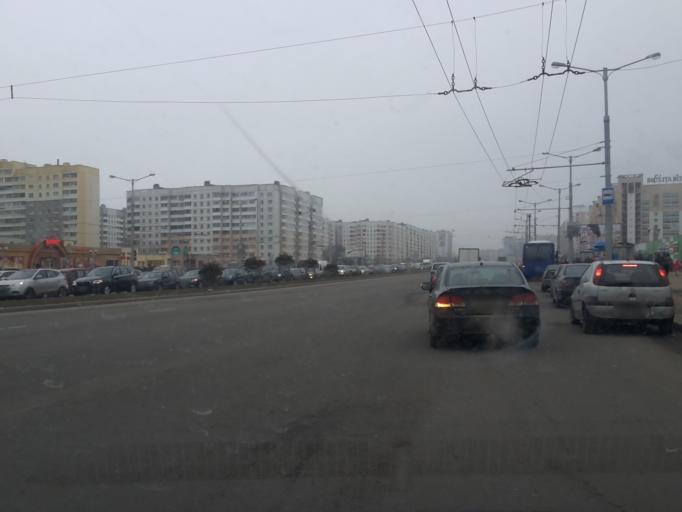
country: BY
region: Minsk
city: Novoye Medvezhino
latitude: 53.9068
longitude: 27.4364
